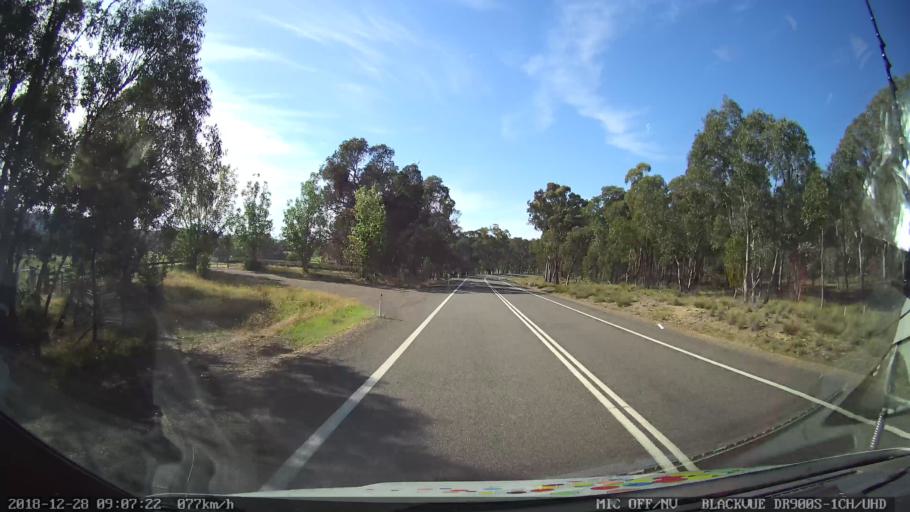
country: AU
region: New South Wales
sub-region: Upper Lachlan Shire
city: Crookwell
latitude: -34.2059
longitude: 149.3447
